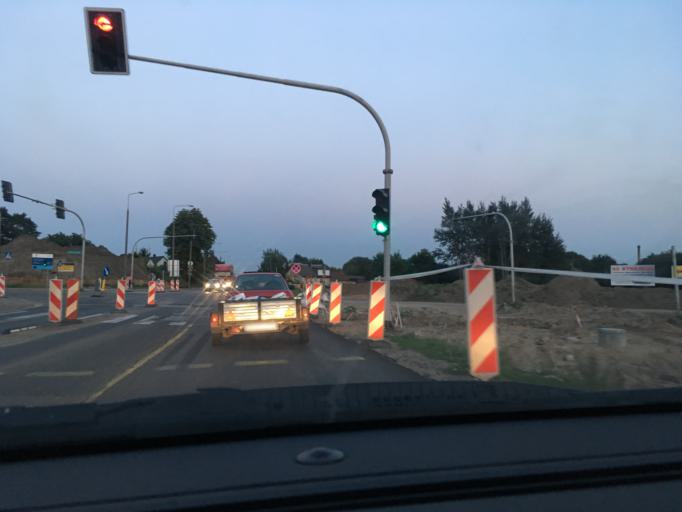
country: PL
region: Podlasie
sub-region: Bialystok
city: Bialystok
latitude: 53.1206
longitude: 23.1957
